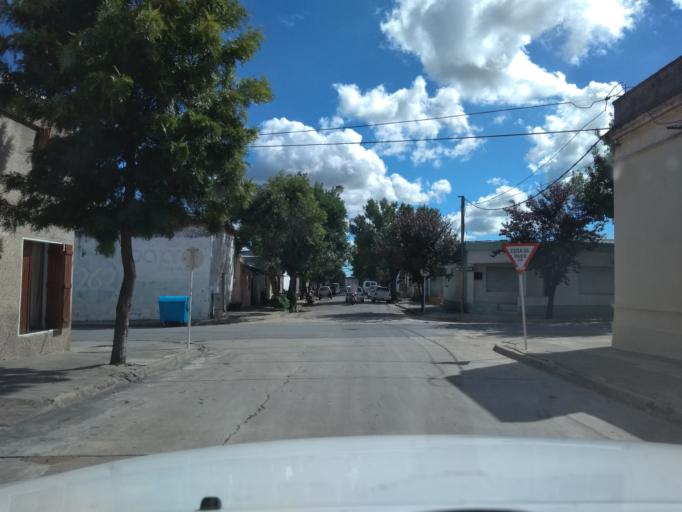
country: UY
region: Florida
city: Florida
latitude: -34.1028
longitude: -56.2161
